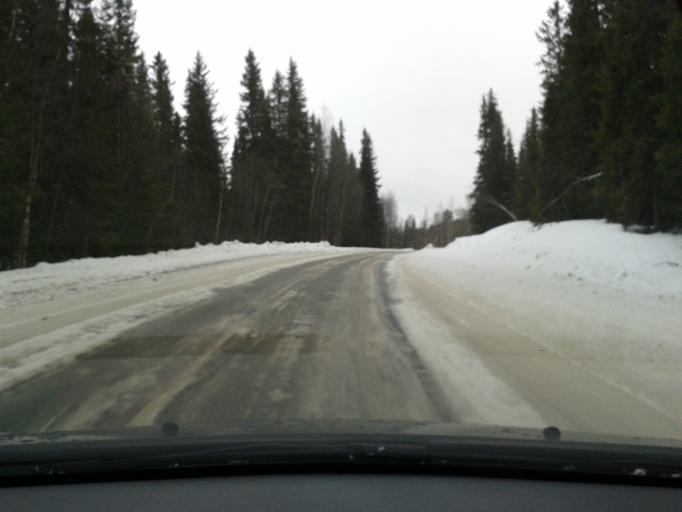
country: SE
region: Vaesterbotten
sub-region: Vilhelmina Kommun
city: Sjoberg
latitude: 64.6556
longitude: 16.3190
